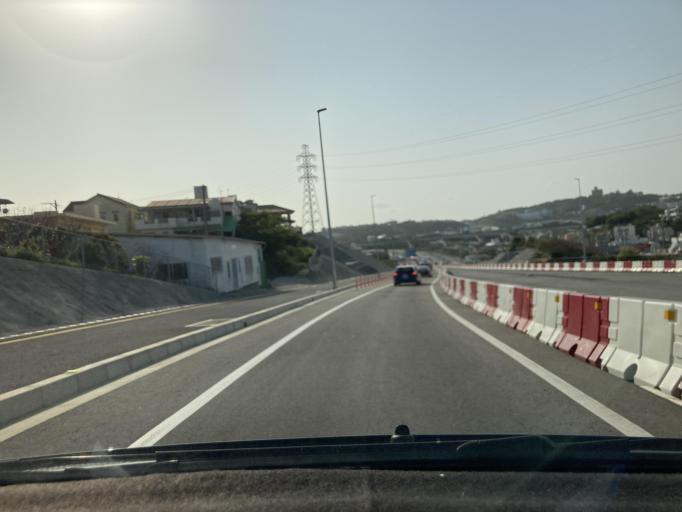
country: JP
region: Okinawa
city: Ginowan
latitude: 26.2024
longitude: 127.7455
